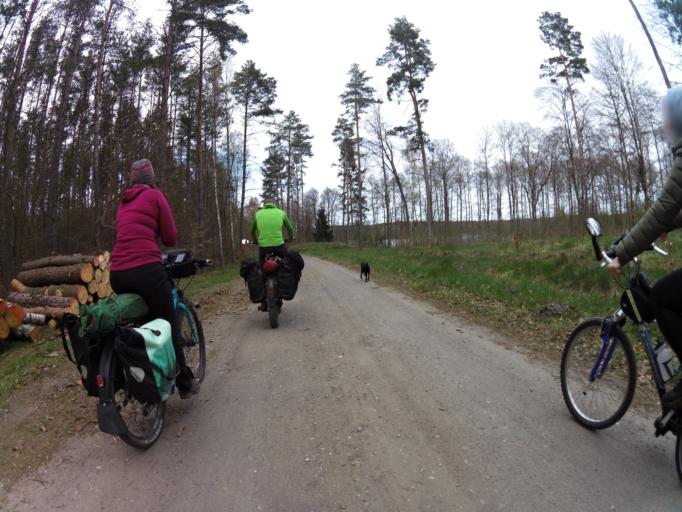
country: PL
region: West Pomeranian Voivodeship
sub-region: Powiat koszalinski
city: Bobolice
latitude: 53.8629
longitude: 16.6849
